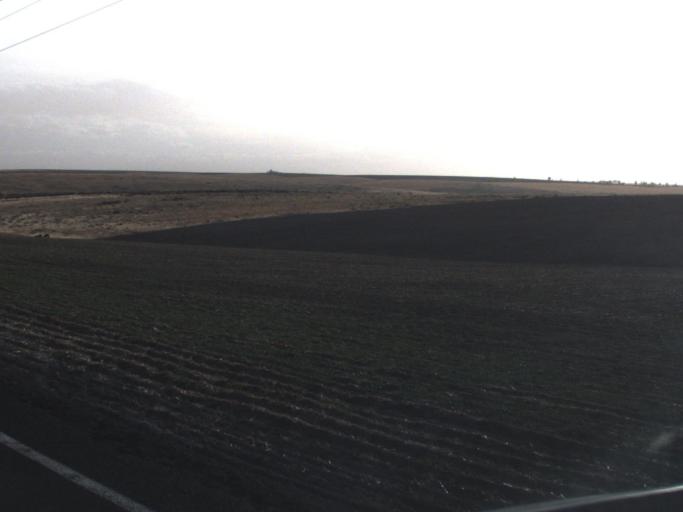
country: US
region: Washington
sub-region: Adams County
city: Ritzville
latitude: 47.2344
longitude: -118.6862
